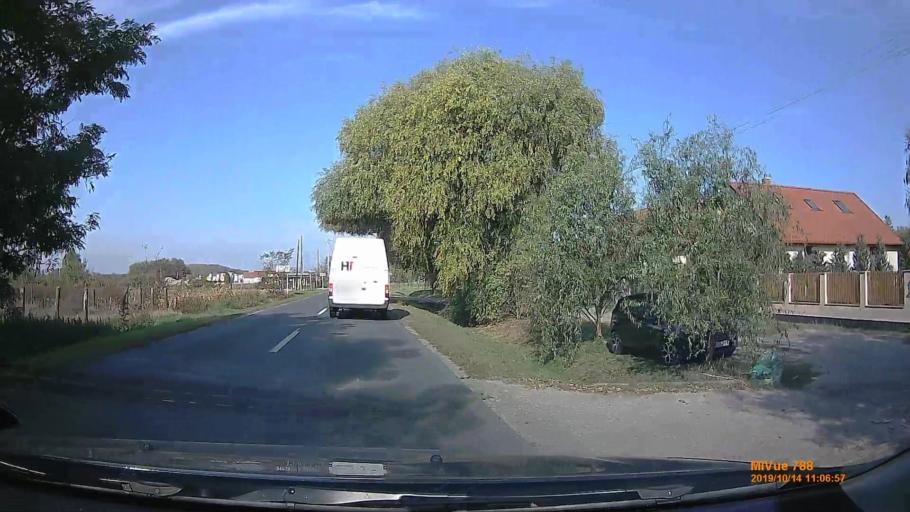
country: HU
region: Pest
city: Monor
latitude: 47.3629
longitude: 19.4306
